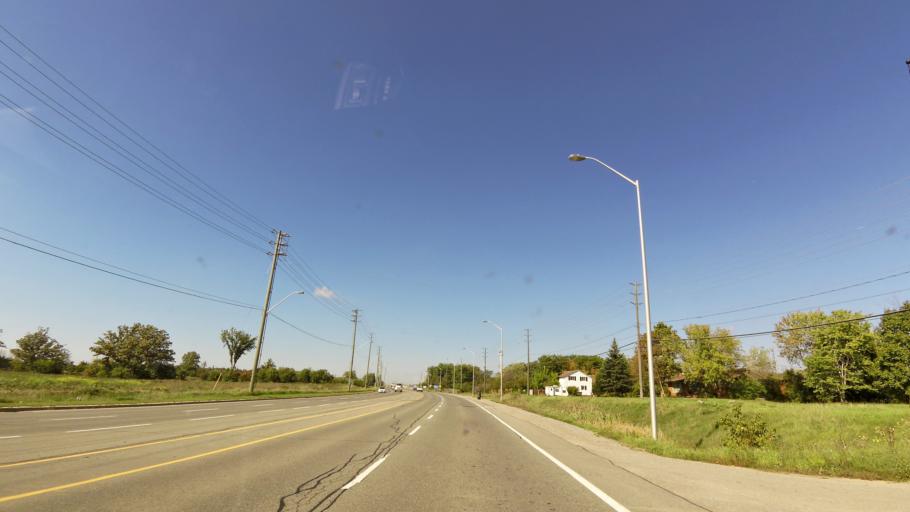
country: CA
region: Ontario
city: Burlington
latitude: 43.4396
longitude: -79.7823
